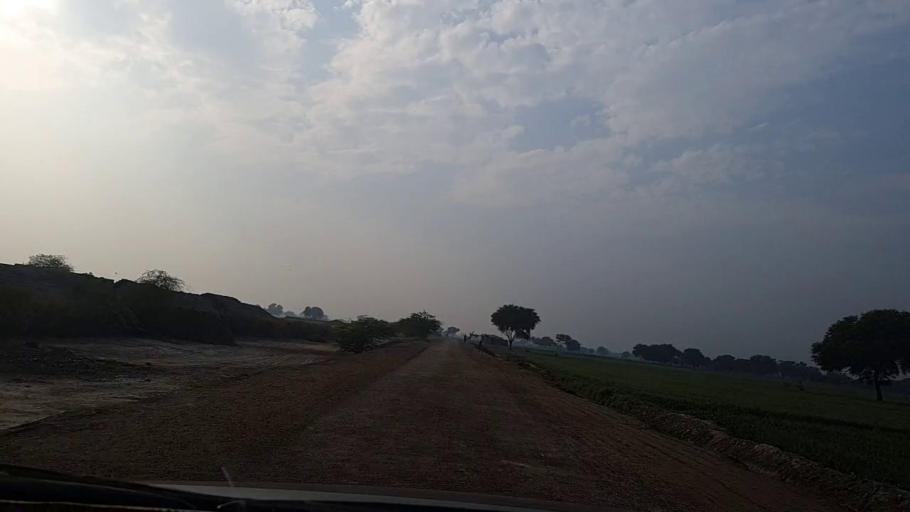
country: PK
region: Sindh
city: Nawabshah
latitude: 26.2738
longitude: 68.3341
